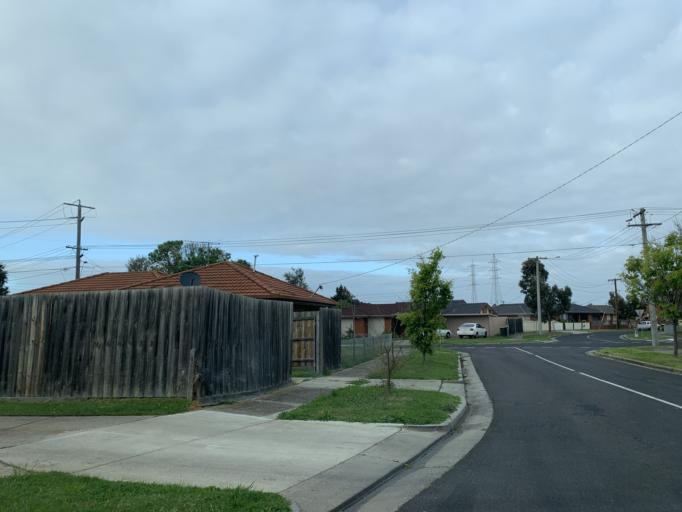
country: AU
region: Victoria
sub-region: Brimbank
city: Kealba
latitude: -37.7508
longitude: 144.8221
